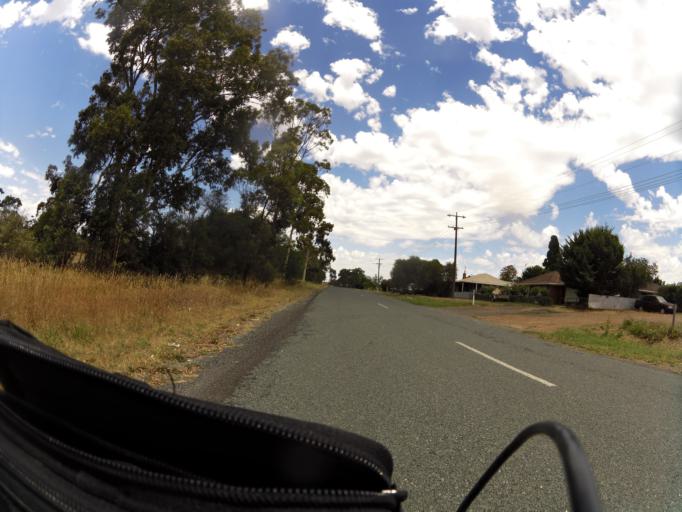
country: AU
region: Victoria
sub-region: Greater Shepparton
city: Shepparton
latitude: -36.6231
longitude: 145.2150
